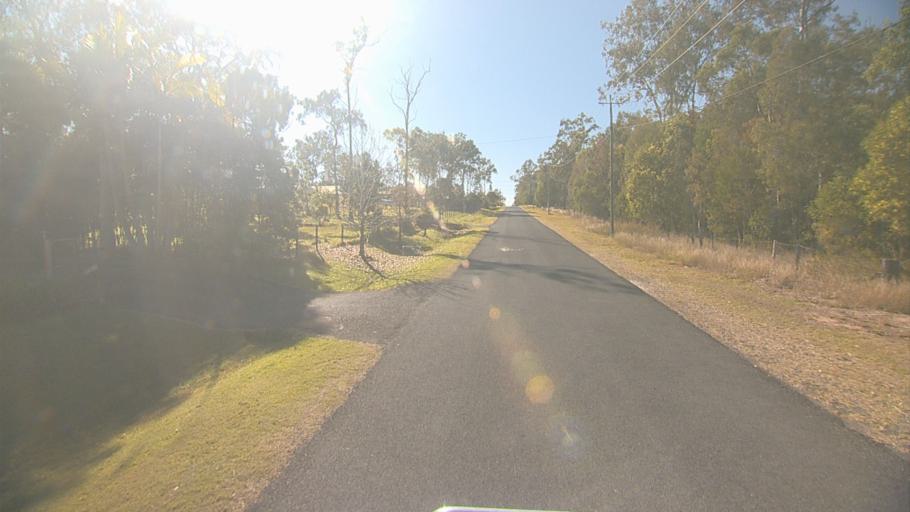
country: AU
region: Queensland
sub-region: Logan
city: Park Ridge South
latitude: -27.7457
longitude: 153.0383
